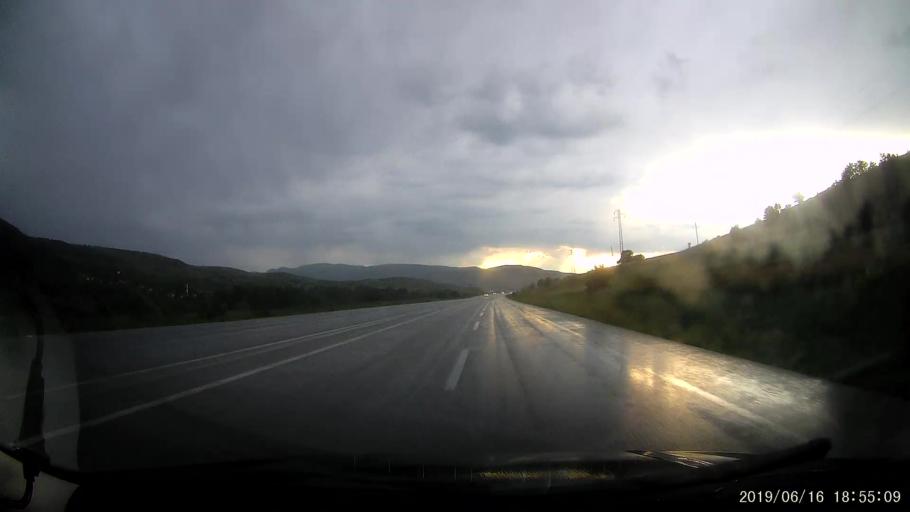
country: TR
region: Erzincan
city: Refahiye
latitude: 39.8991
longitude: 38.8354
